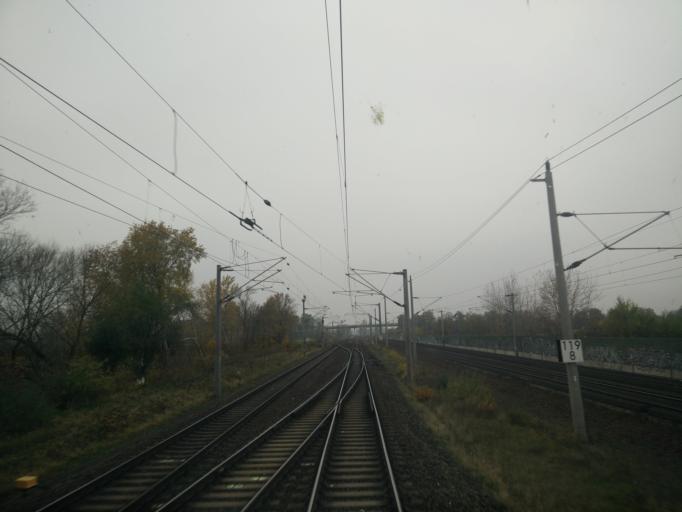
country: DE
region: Brandenburg
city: Falkensee
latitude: 52.5409
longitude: 13.0957
